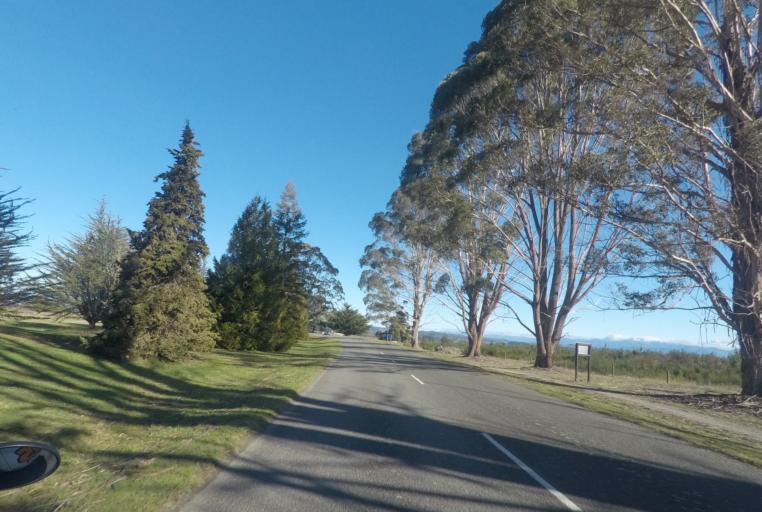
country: NZ
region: Tasman
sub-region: Tasman District
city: Mapua
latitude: -41.2818
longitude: 173.1351
